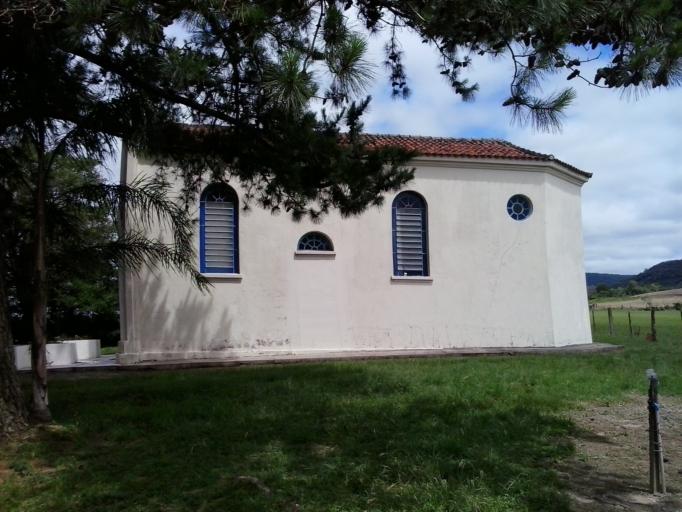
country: BR
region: Rio Grande do Sul
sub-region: Santa Maria
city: Santa Maria
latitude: -29.7222
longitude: -53.5488
